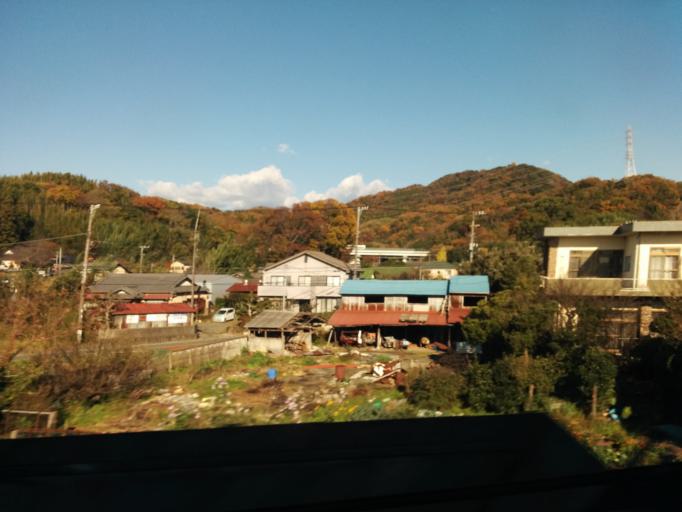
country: JP
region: Kanagawa
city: Oiso
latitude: 35.3184
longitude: 139.2786
